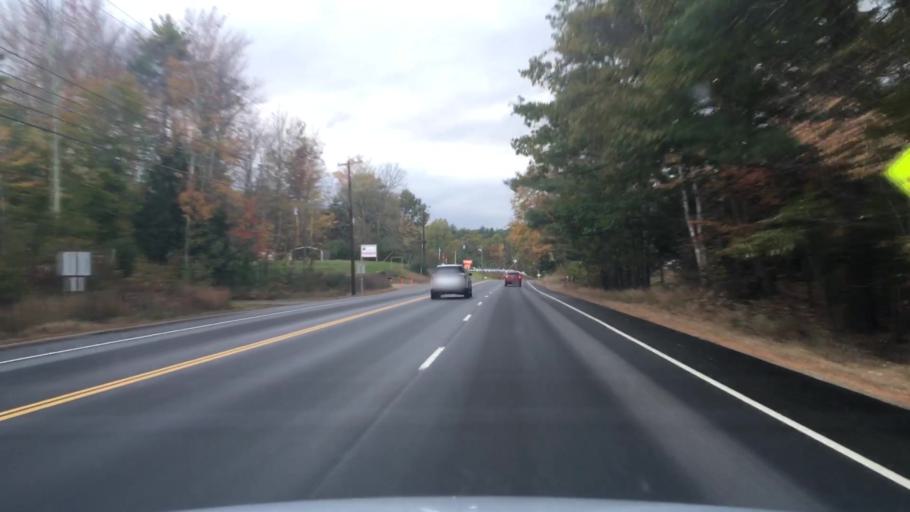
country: US
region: New Hampshire
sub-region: Merrimack County
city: Chichester
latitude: 43.2334
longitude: -71.3807
